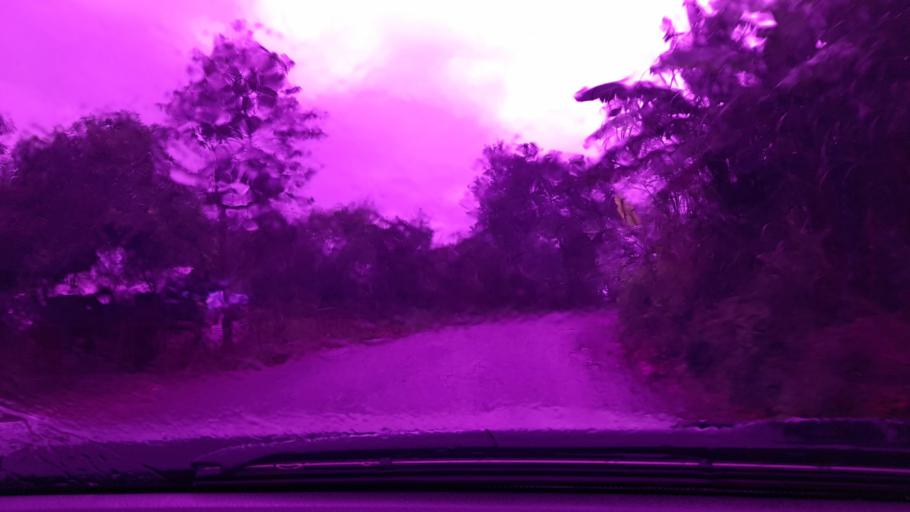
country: ET
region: Oromiya
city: Metu
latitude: 8.3776
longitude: 35.6002
